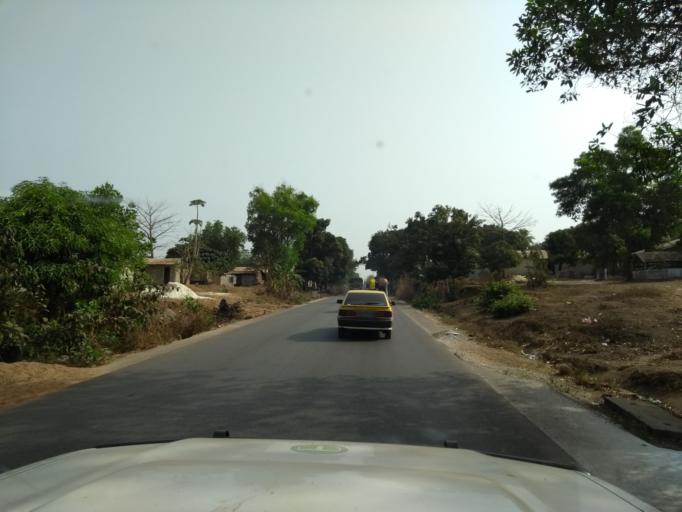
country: GN
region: Kindia
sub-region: Prefecture de Dubreka
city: Dubreka
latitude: 9.8478
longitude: -13.4856
